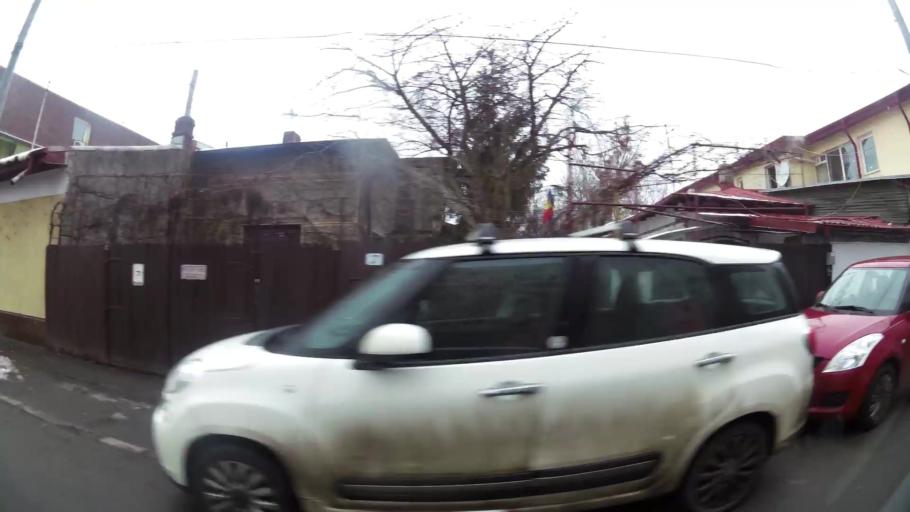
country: RO
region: Ilfov
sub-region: Comuna Chiajna
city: Rosu
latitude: 44.4572
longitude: 26.0439
